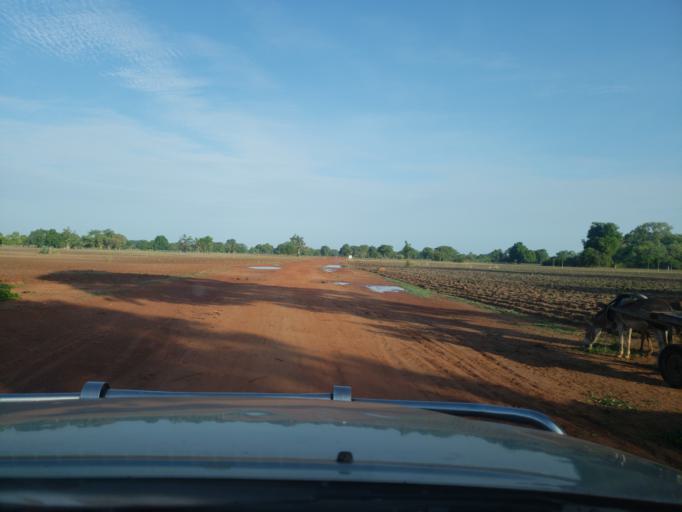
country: ML
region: Sikasso
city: Koutiala
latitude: 12.4060
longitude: -5.5423
